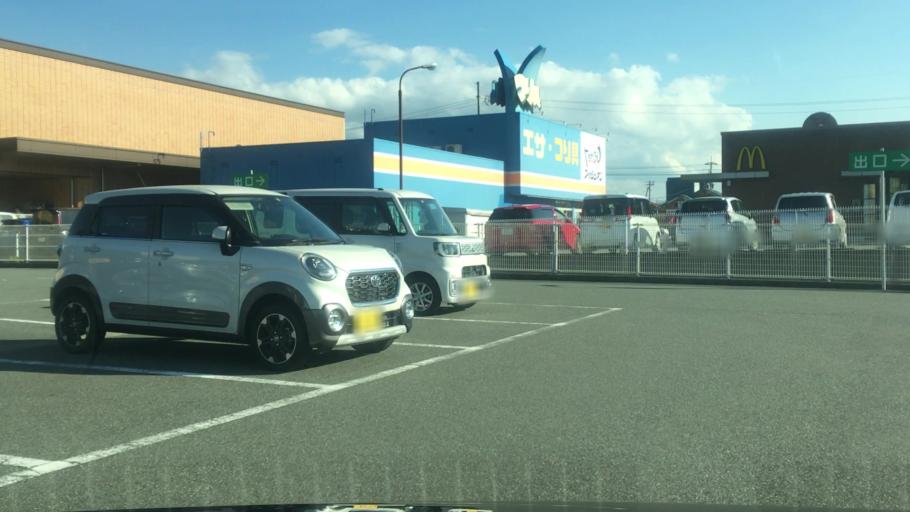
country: JP
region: Hyogo
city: Toyooka
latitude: 35.5549
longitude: 134.8133
